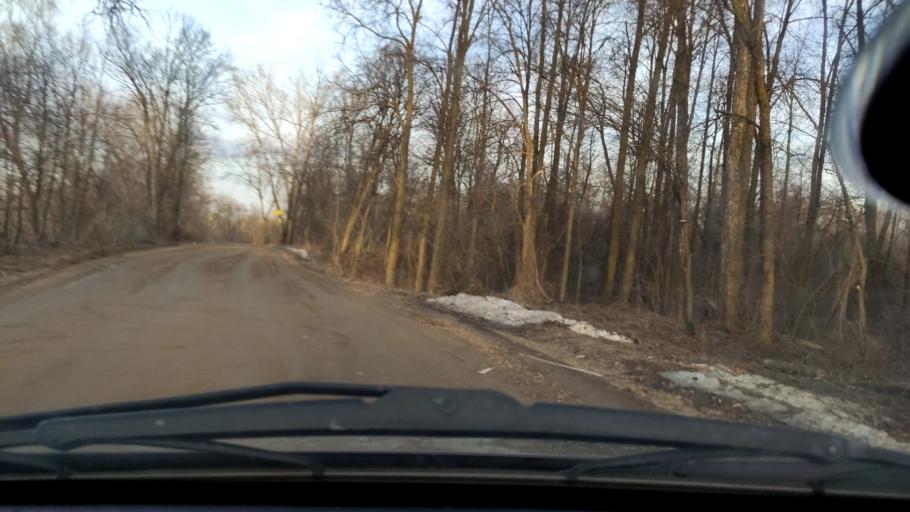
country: RU
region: Bashkortostan
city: Ufa
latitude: 54.7960
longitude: 56.1875
